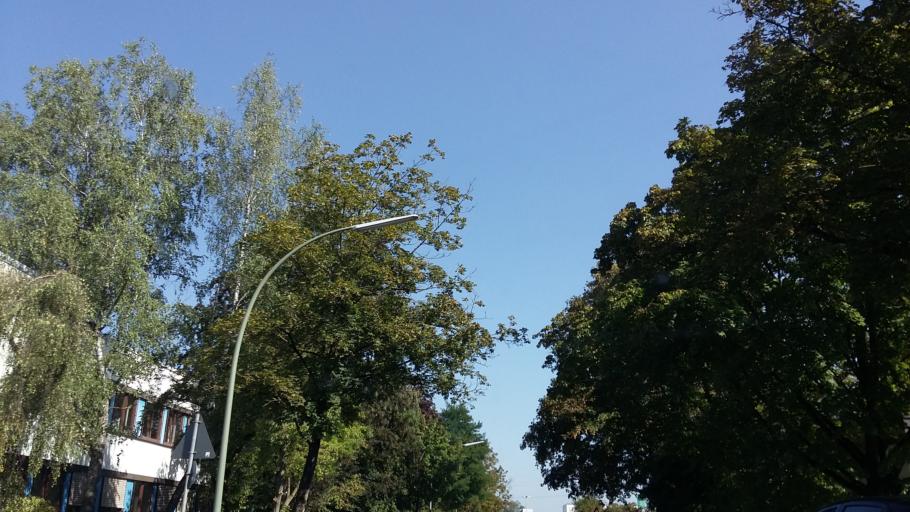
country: DE
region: Bavaria
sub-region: Swabia
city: Augsburg
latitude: 48.3481
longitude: 10.8830
